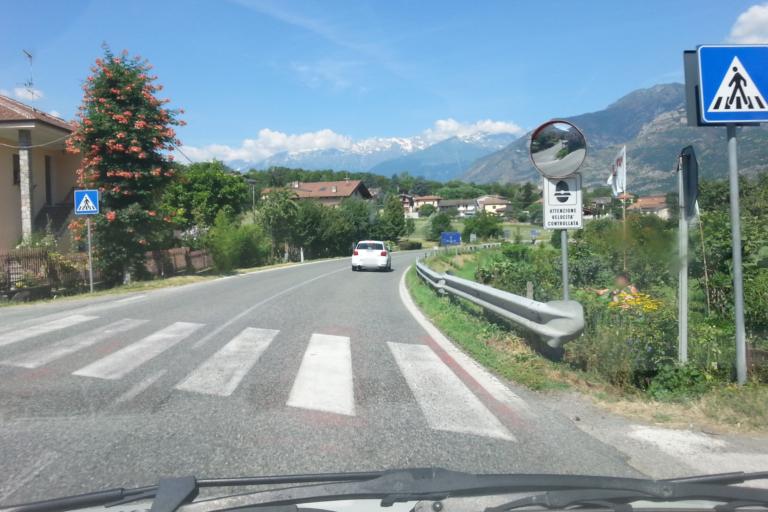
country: IT
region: Piedmont
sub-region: Provincia di Torino
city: San Giorio
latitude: 45.1271
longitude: 7.1779
